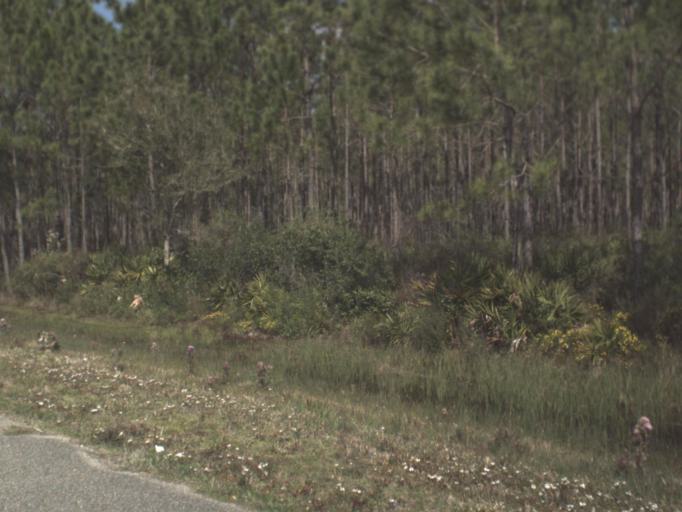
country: US
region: Florida
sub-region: Franklin County
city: Apalachicola
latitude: 29.7267
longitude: -85.1278
